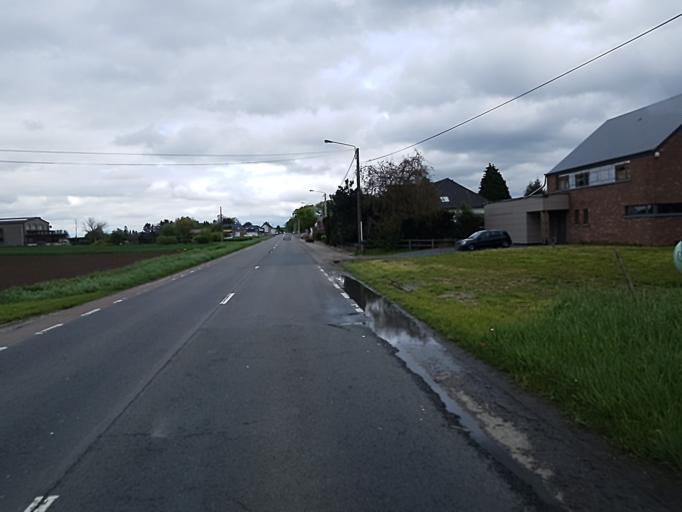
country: BE
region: Wallonia
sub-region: Province de Namur
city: Gembloux
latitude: 50.5845
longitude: 4.7133
